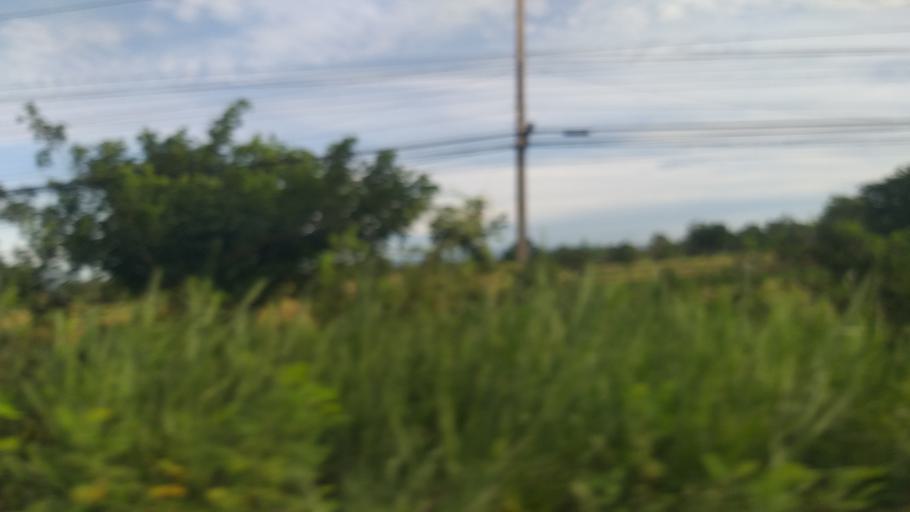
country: TH
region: Chaiyaphum
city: Ban Thaen
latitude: 16.3928
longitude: 102.3305
